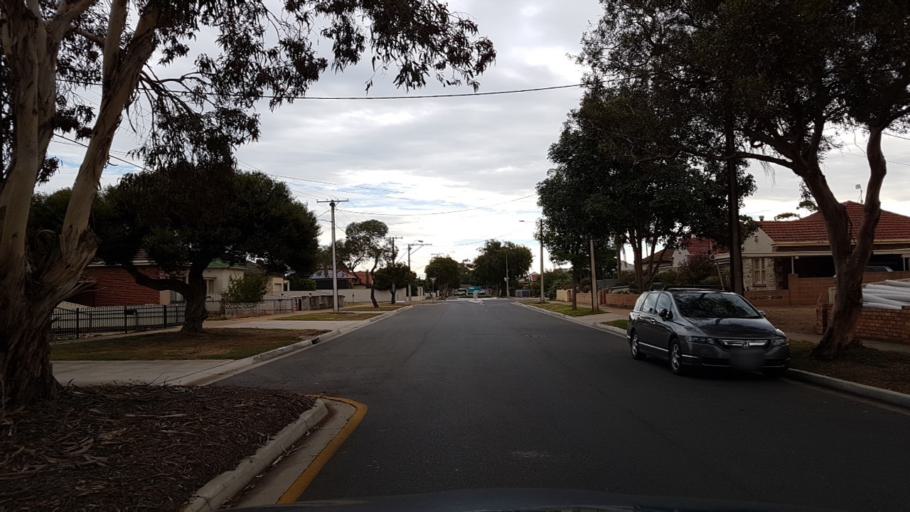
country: AU
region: South Australia
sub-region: Port Adelaide Enfield
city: Alberton
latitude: -34.8591
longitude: 138.5326
